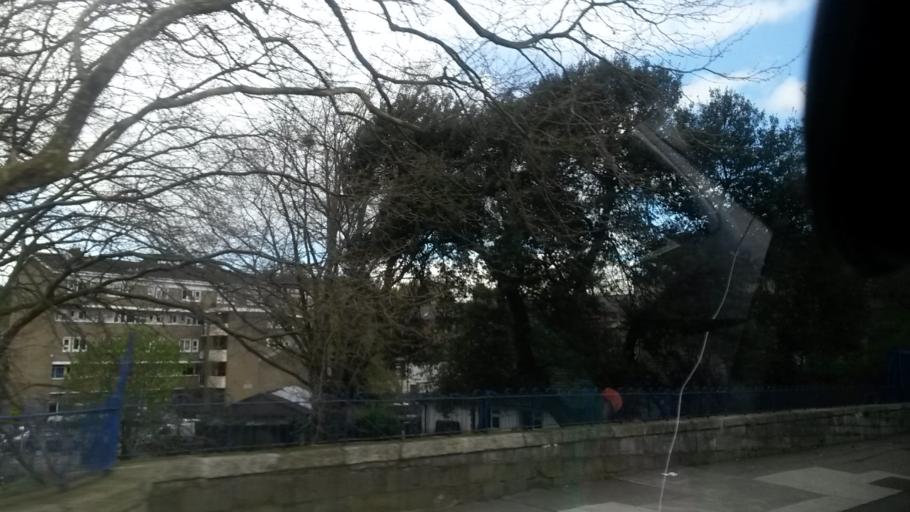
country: IE
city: Greenhills
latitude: 53.3475
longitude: -6.3083
